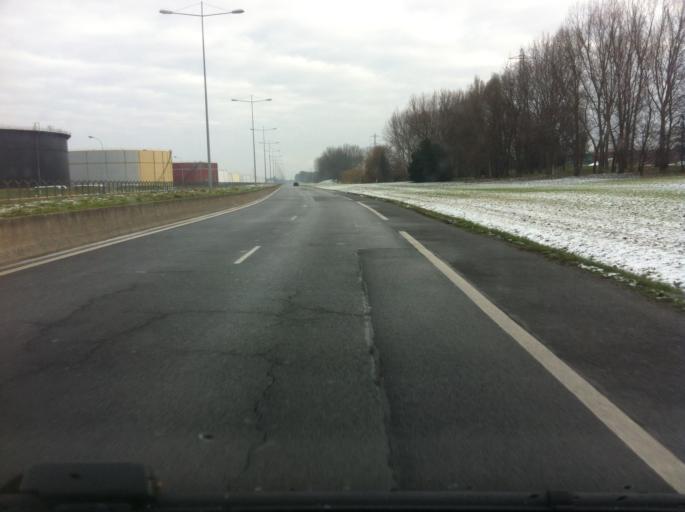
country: FR
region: Haute-Normandie
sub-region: Departement de la Seine-Maritime
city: Rogerville
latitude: 49.4831
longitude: 0.2341
